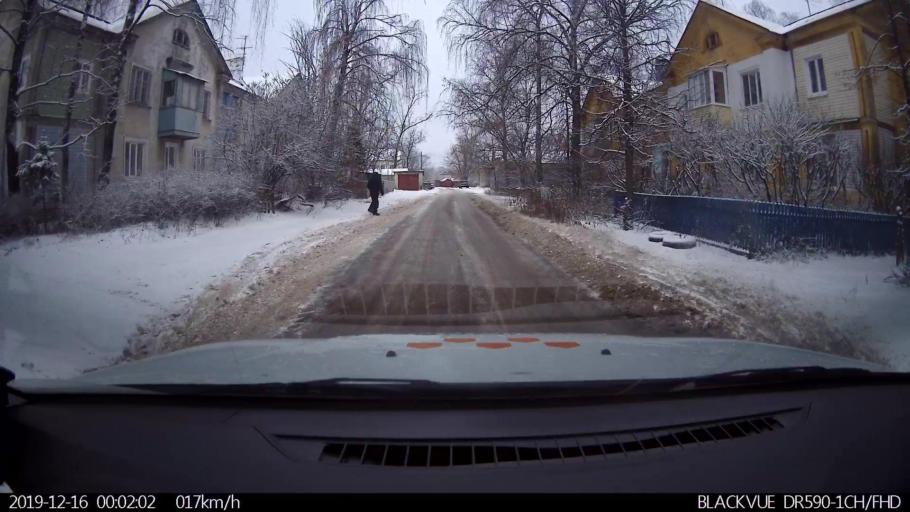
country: RU
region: Nizjnij Novgorod
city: Gorbatovka
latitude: 56.3586
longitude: 43.8440
